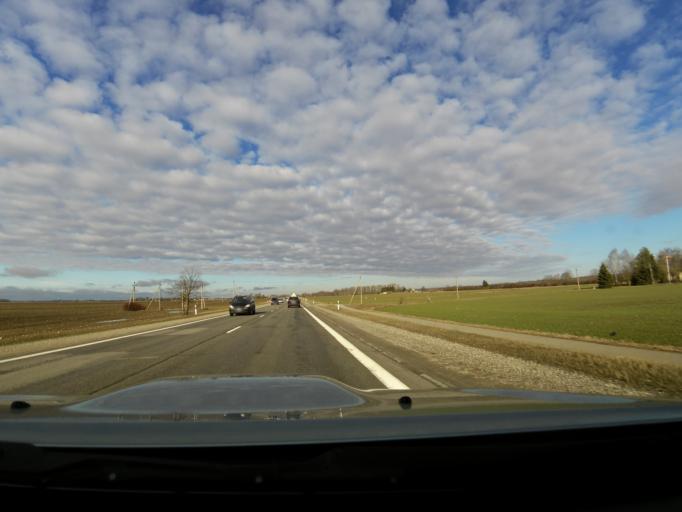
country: LT
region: Panevezys
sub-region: Panevezys City
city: Panevezys
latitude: 55.7379
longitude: 24.2007
